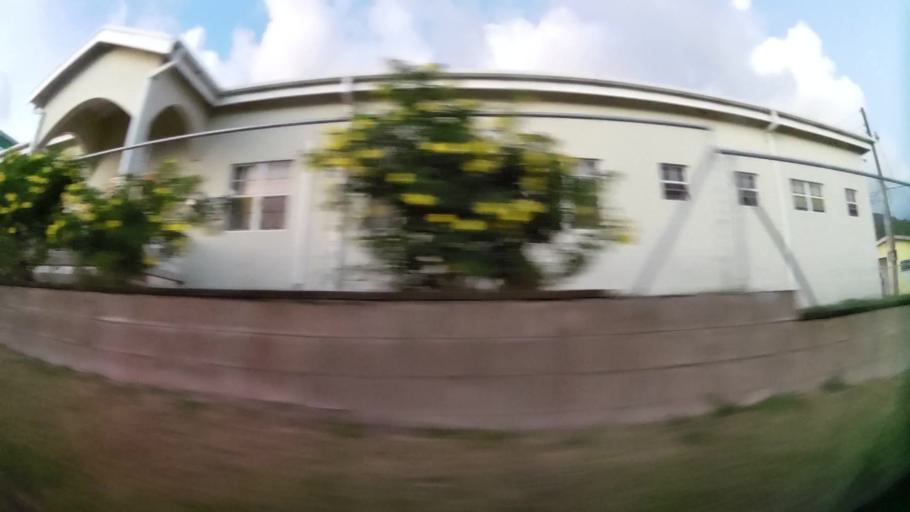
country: KN
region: Saint Thomas Middle Island
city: Middle Island
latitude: 17.3222
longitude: -62.8036
